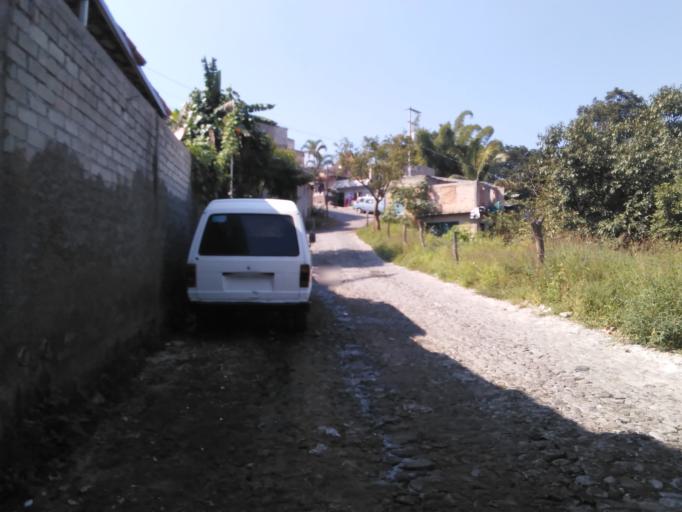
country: MX
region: Nayarit
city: Tepic
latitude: 21.5302
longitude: -104.9175
